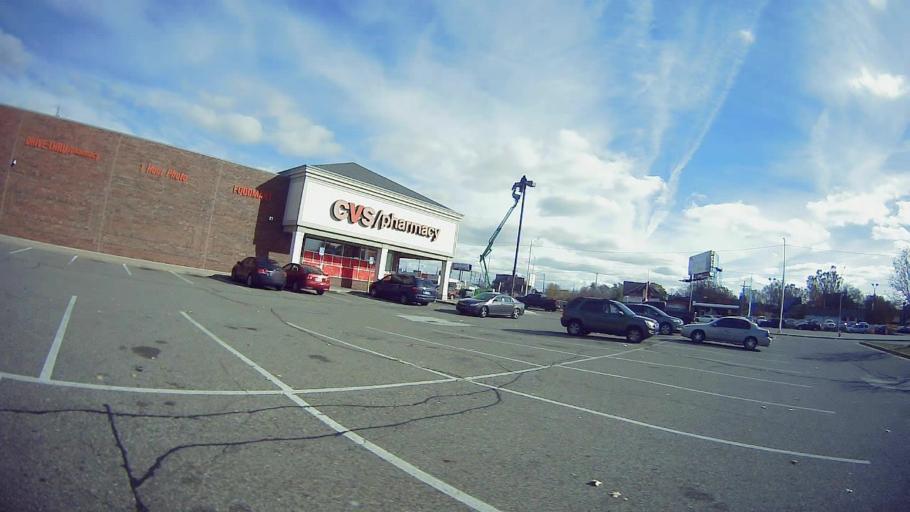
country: US
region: Michigan
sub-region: Macomb County
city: Eastpointe
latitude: 42.4490
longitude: -82.9695
